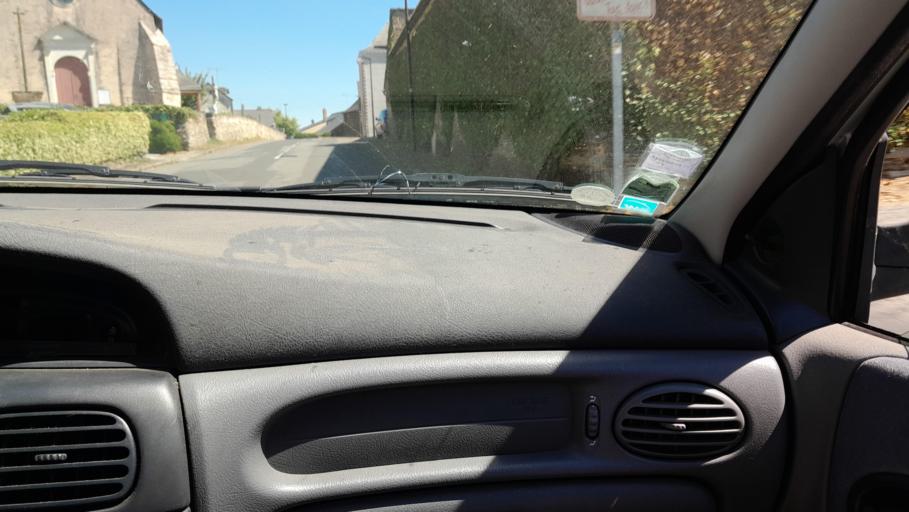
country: FR
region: Pays de la Loire
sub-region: Departement de Maine-et-Loire
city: Pouance
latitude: 47.7524
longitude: -1.1800
